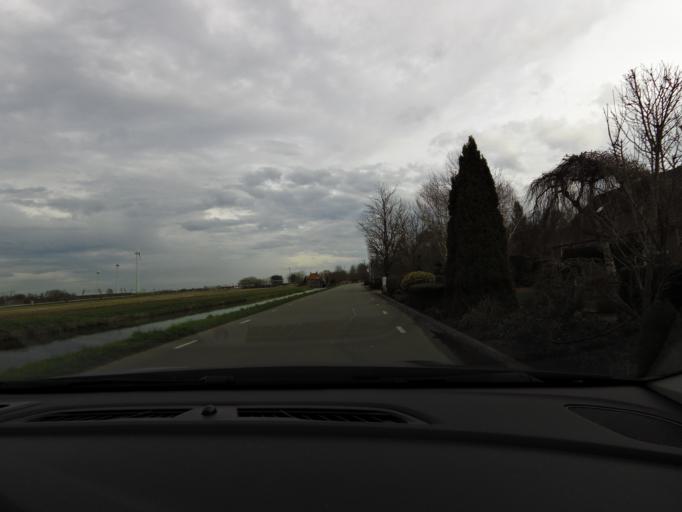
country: NL
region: South Holland
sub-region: Gemeente Hardinxveld-Giessendam
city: Boven-Hardinxveld
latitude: 51.8331
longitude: 4.8718
